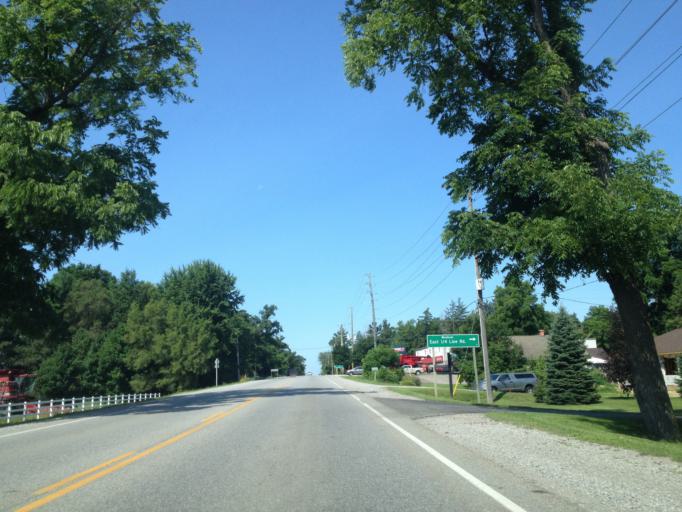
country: CA
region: Ontario
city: Norfolk County
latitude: 42.8382
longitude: -80.3484
